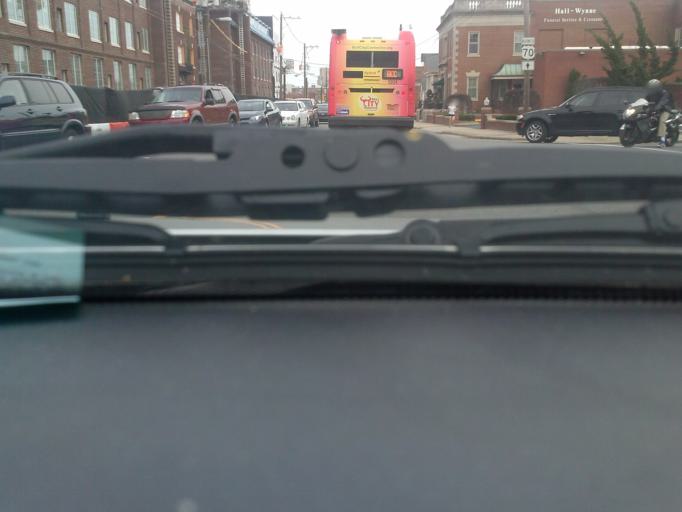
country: US
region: North Carolina
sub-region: Durham County
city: Durham
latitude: 36.0020
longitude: -78.9126
